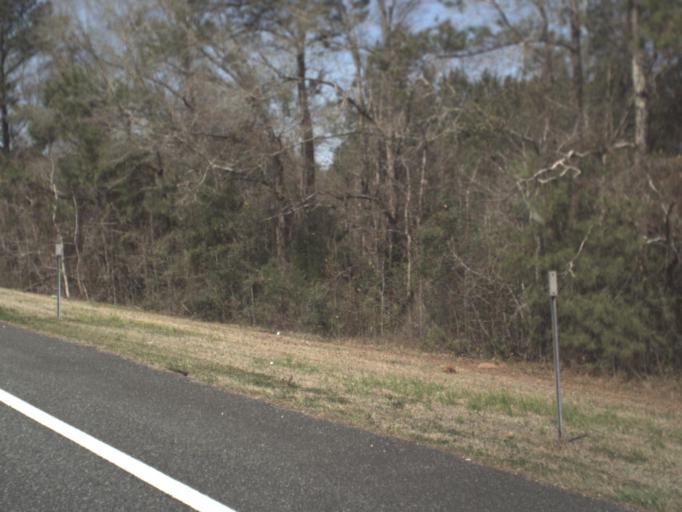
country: US
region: Florida
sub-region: Jackson County
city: Marianna
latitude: 30.7578
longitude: -85.3174
